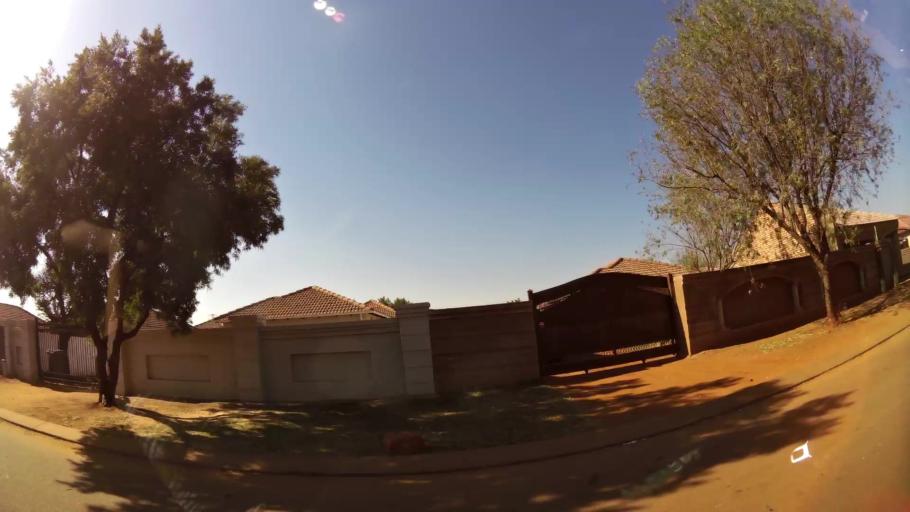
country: ZA
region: North-West
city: Ga-Rankuwa
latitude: -25.6347
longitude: 28.0788
